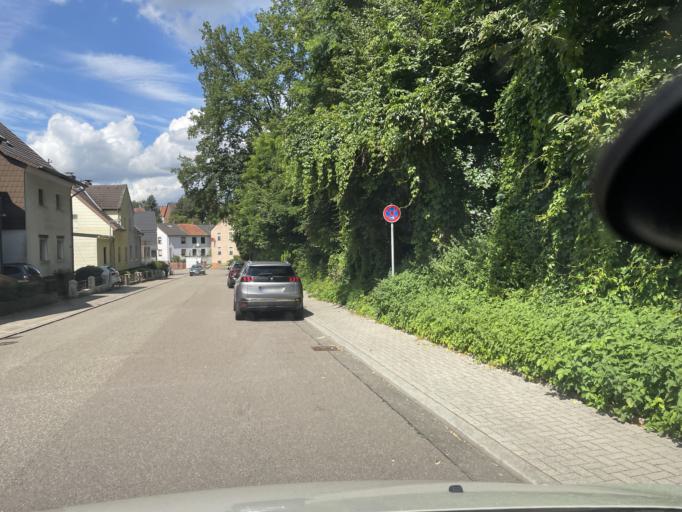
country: DE
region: Saarland
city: Sulzbach
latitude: 49.2725
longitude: 7.0470
